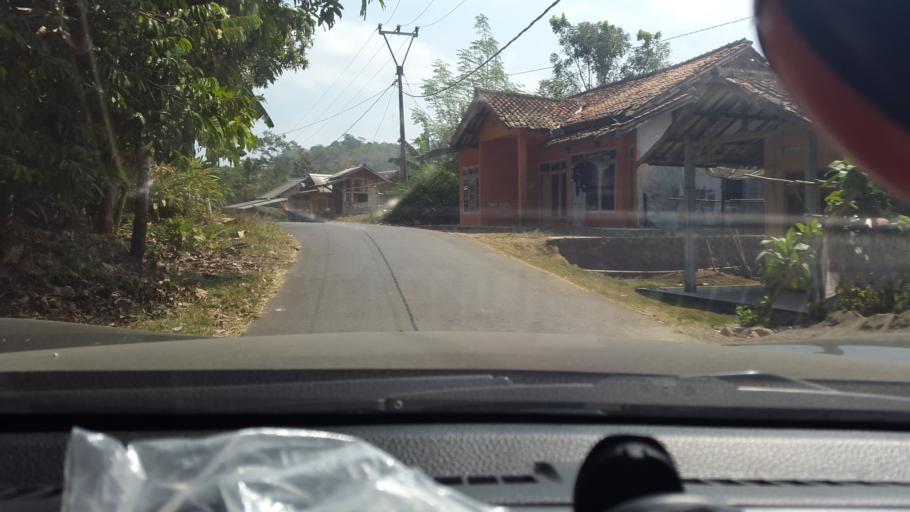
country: ID
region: West Java
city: Buniwangi
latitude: -7.2797
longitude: 106.8018
